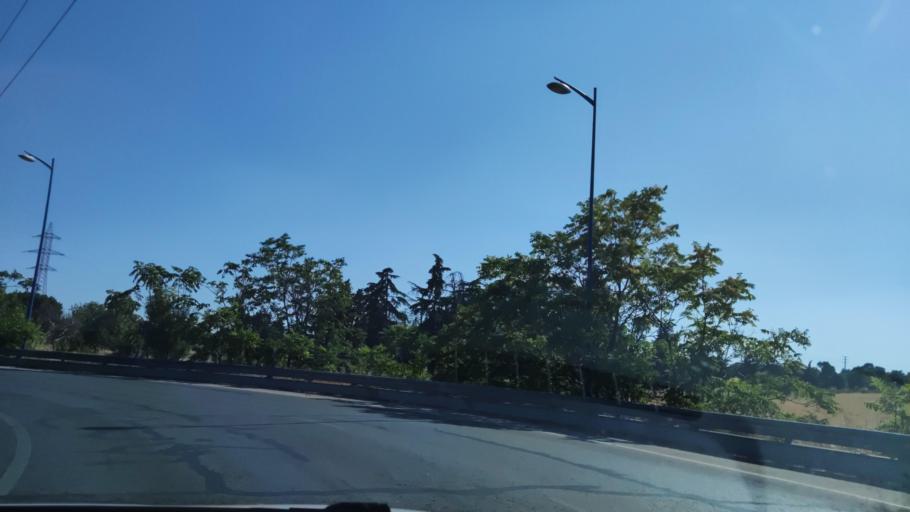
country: ES
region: Madrid
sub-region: Provincia de Madrid
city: Leganes
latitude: 40.3407
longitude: -3.7877
